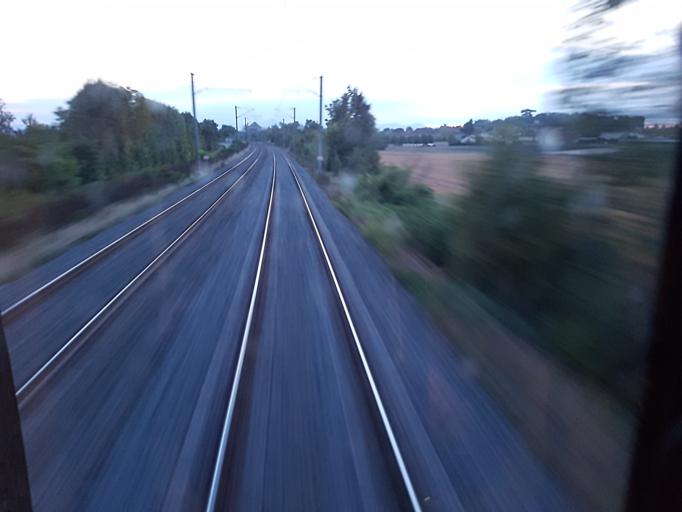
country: FR
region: Auvergne
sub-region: Departement du Puy-de-Dome
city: Maringues
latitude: 45.9699
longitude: 3.2669
